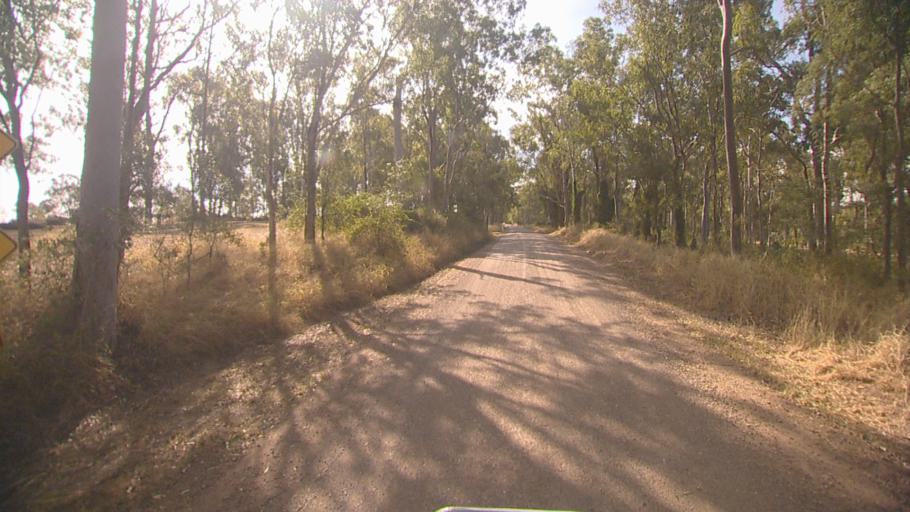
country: AU
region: Queensland
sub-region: Logan
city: Cedar Vale
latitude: -27.9063
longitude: 152.9858
